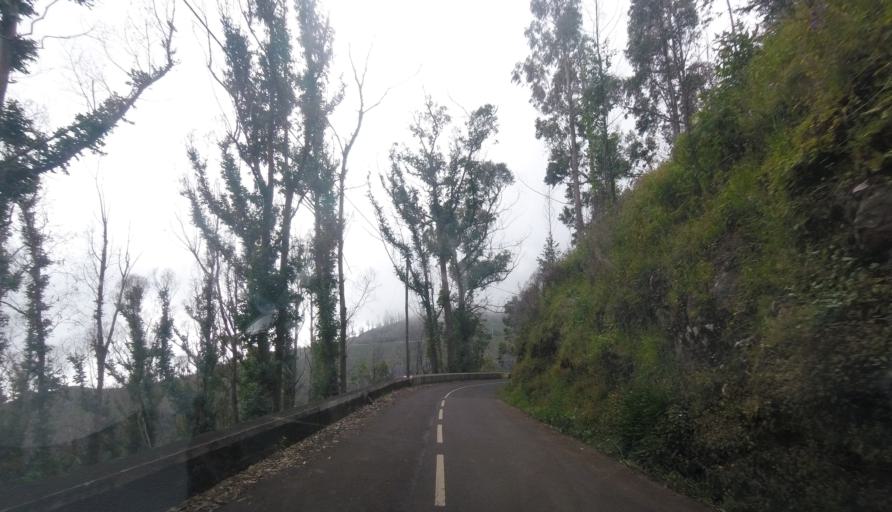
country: PT
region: Madeira
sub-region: Funchal
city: Nossa Senhora do Monte
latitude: 32.6830
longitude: -16.8911
